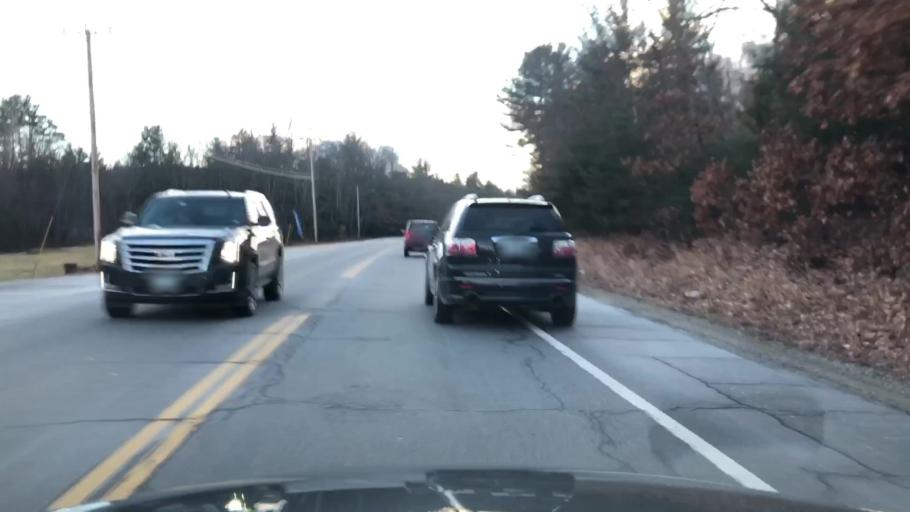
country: US
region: New Hampshire
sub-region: Hillsborough County
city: Milford
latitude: 42.8087
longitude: -71.6485
